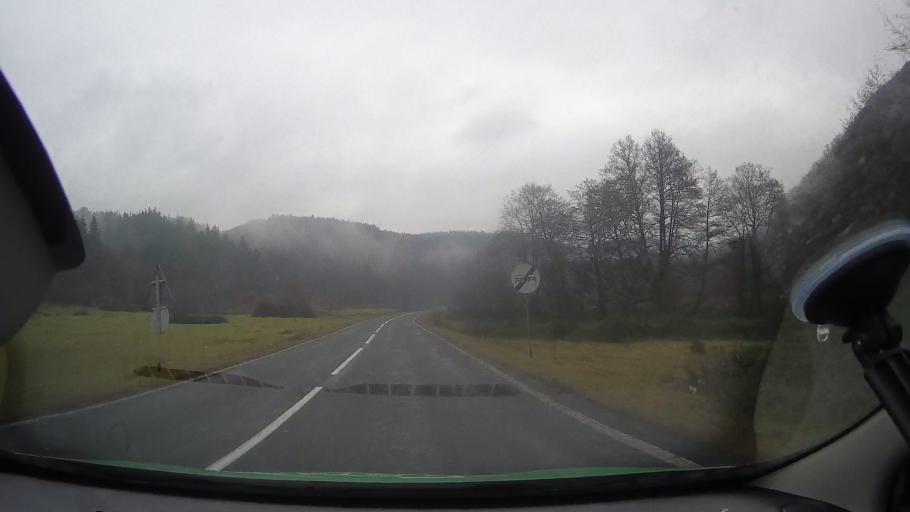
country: RO
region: Arad
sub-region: Comuna Plescuta
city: Plescuta
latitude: 46.3160
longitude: 22.4570
